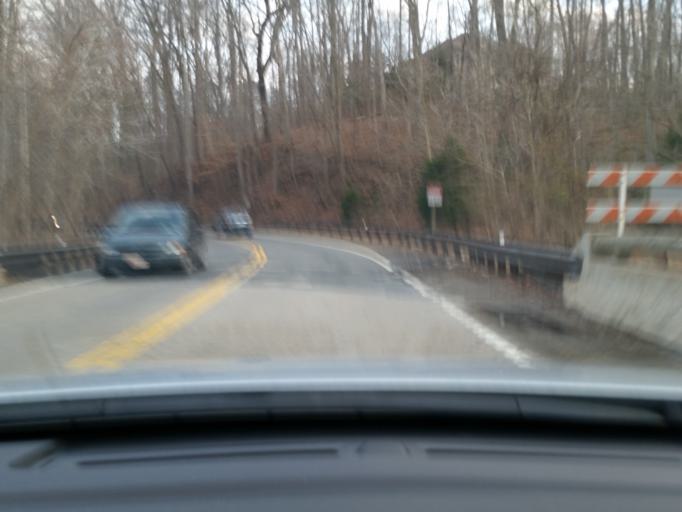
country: US
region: Virginia
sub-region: Fairfax County
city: Great Falls
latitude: 38.9758
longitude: -77.2460
